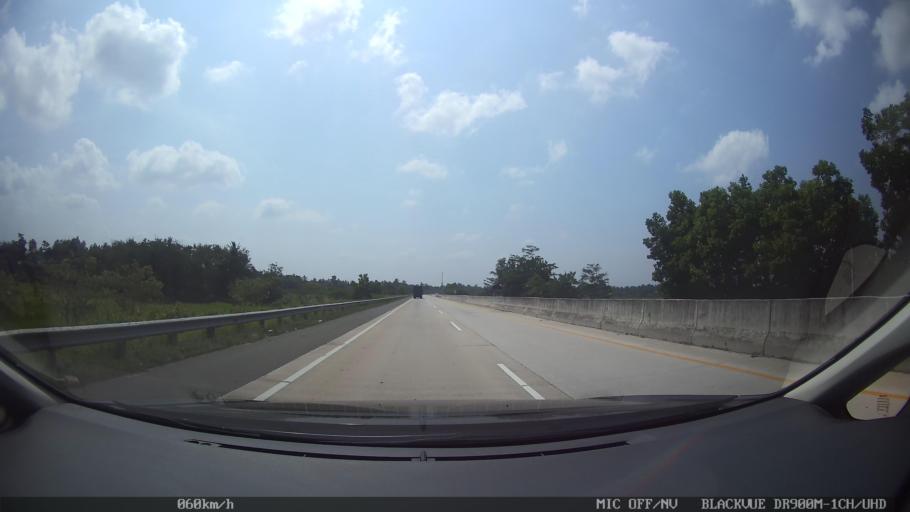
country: ID
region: Lampung
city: Natar
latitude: -5.2921
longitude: 105.2305
